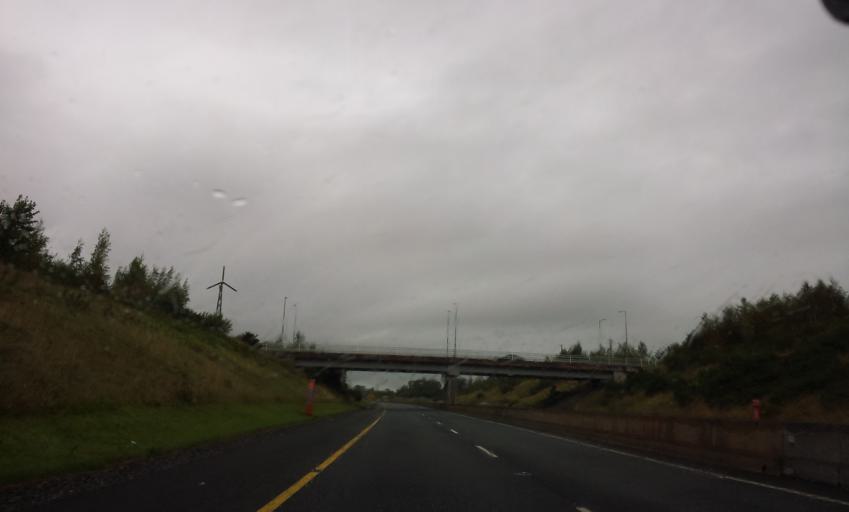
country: IE
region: Munster
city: Cahir
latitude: 52.3985
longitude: -7.9166
